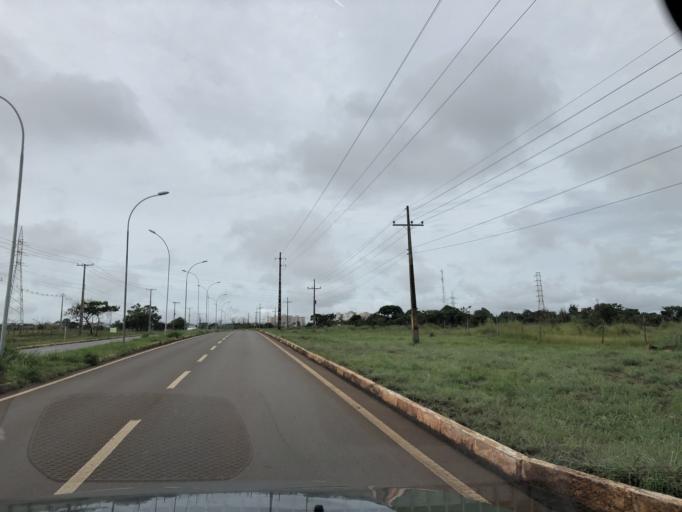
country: BR
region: Federal District
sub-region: Brasilia
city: Brasilia
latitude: -15.7787
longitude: -48.1296
